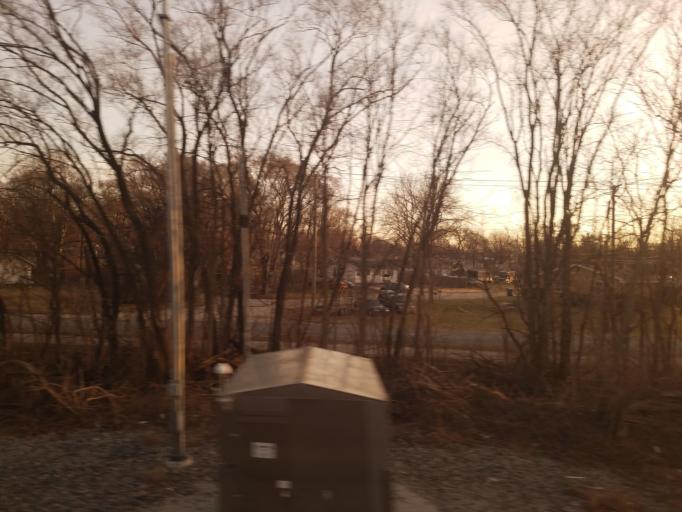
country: US
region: Indiana
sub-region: Elkhart County
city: Dunlap
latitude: 41.6410
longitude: -85.9257
